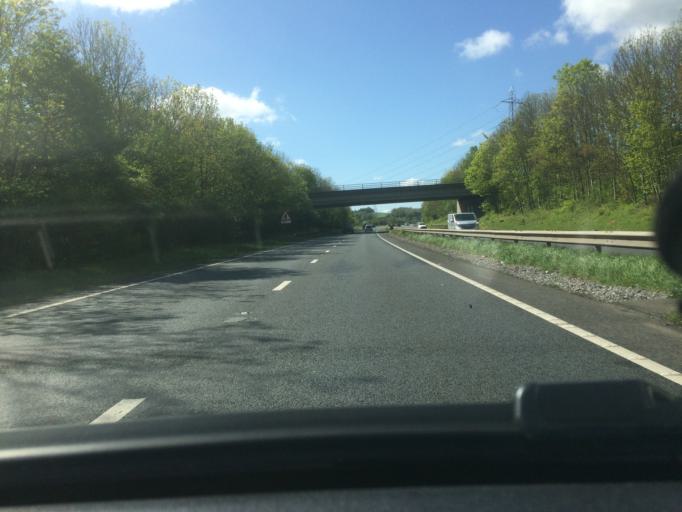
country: GB
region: Wales
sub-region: Wrexham
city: Ruabon
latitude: 53.0058
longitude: -3.0229
